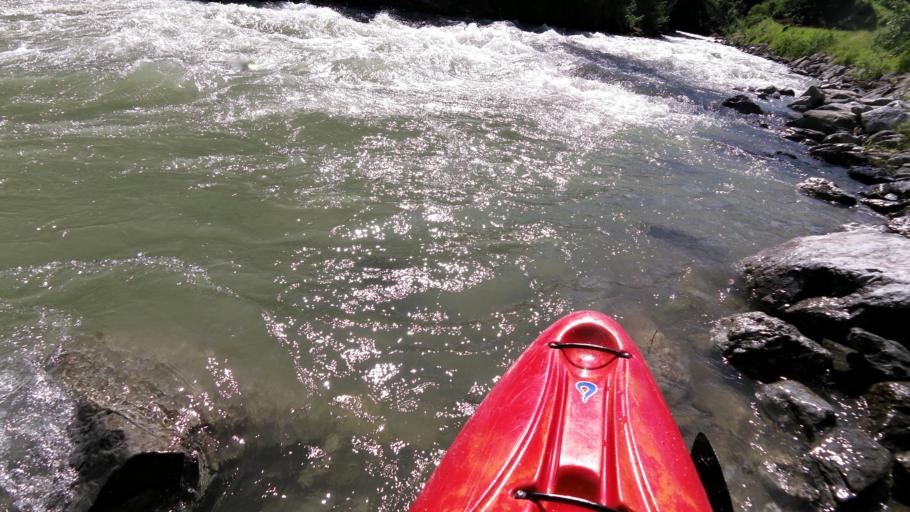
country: AT
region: Tyrol
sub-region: Politischer Bezirk Landeck
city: Strengen
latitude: 47.1261
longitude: 10.4604
